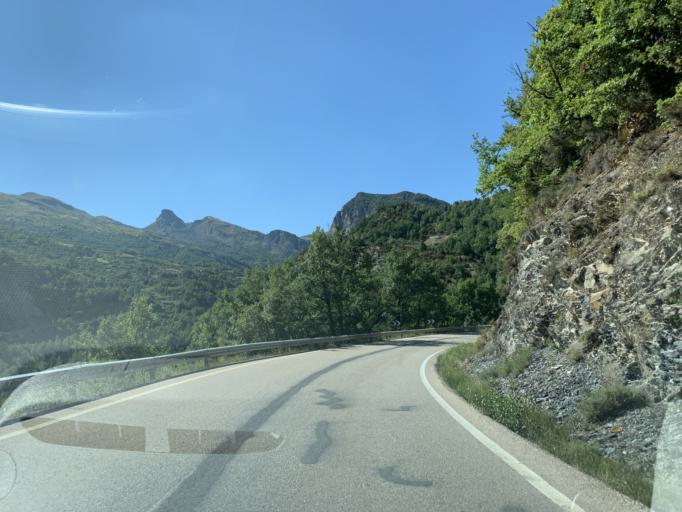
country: ES
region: Aragon
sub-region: Provincia de Huesca
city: Hoz de Jaca
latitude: 42.7281
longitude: -0.3017
